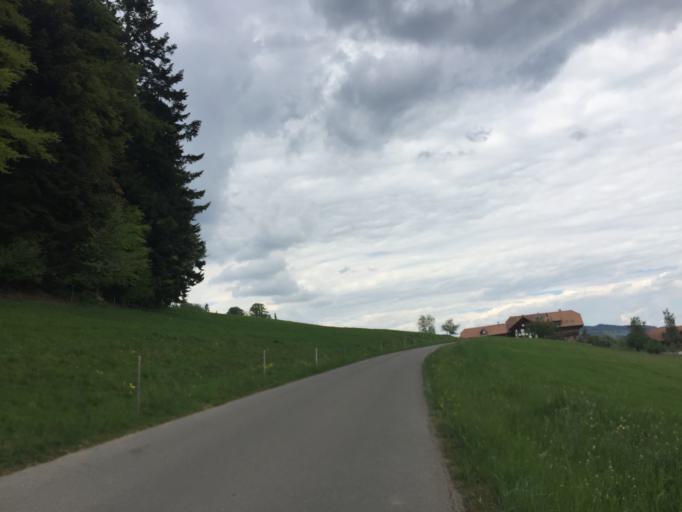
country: CH
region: Bern
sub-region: Thun District
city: Seftigen
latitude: 46.7957
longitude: 7.5557
